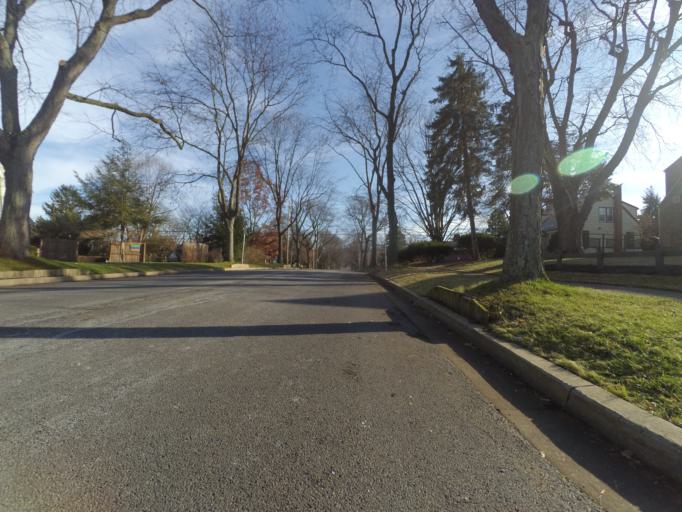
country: US
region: Pennsylvania
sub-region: Centre County
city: State College
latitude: 40.7873
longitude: -77.8475
